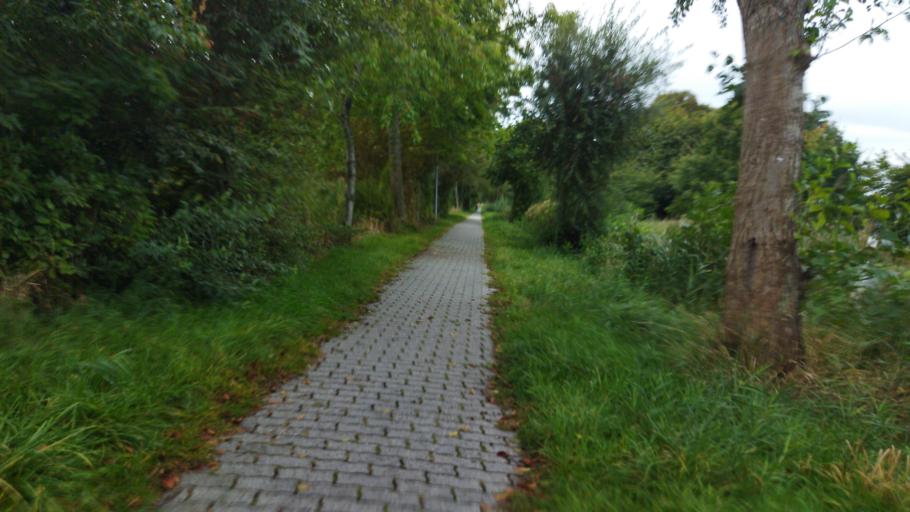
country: DE
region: Lower Saxony
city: Hinte
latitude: 53.4208
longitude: 7.1869
